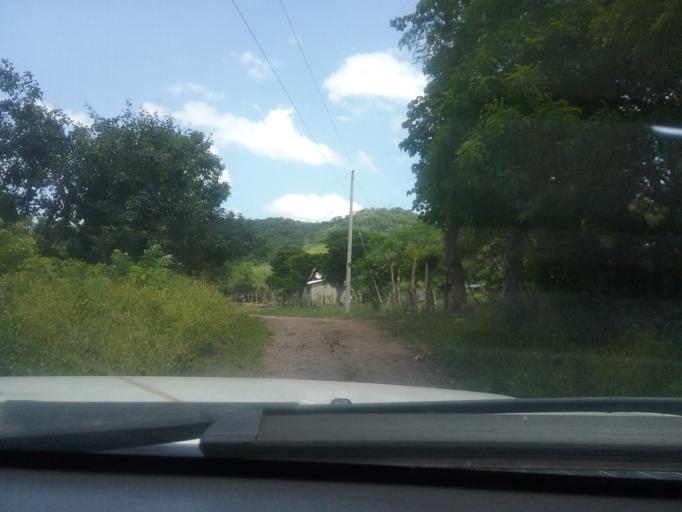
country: NI
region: Matagalpa
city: Terrabona
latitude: 12.6546
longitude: -86.0053
